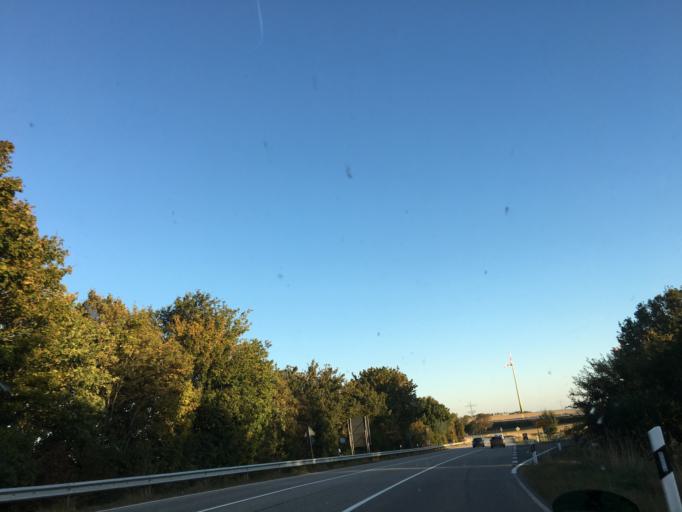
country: DE
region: Rheinland-Pfalz
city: Weselberg
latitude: 49.3317
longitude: 7.6063
